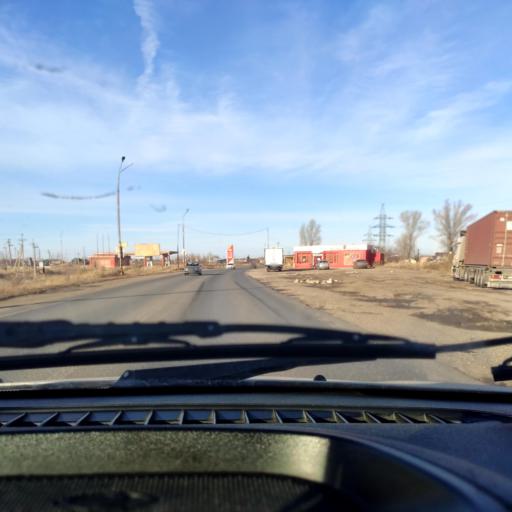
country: RU
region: Samara
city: Tol'yatti
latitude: 53.5707
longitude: 49.3433
